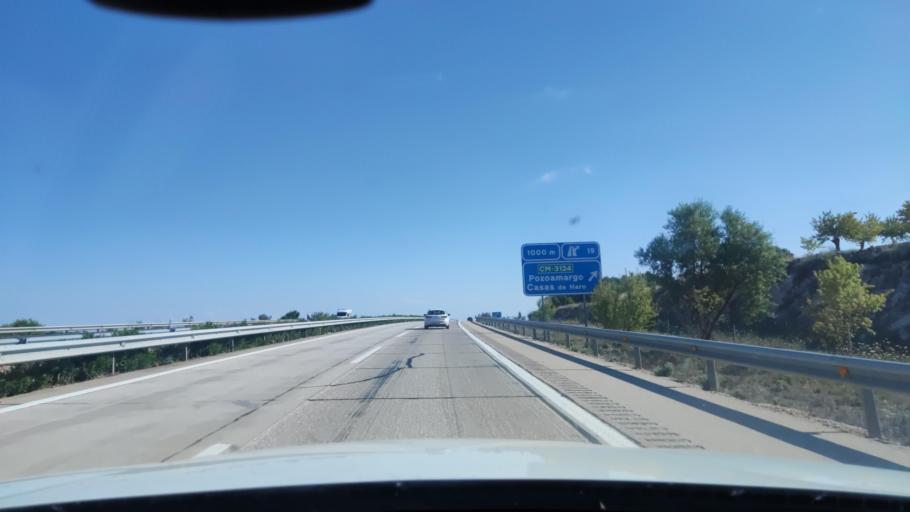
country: ES
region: Castille-La Mancha
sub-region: Provincia de Cuenca
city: Pozoamargo
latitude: 39.3745
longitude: -2.1994
